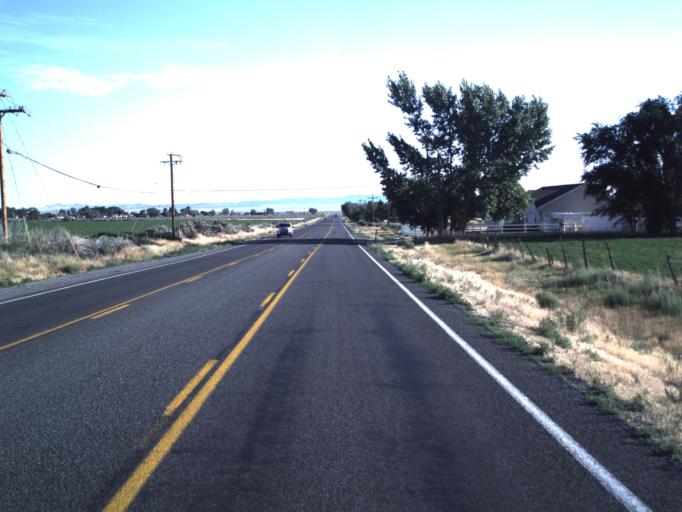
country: US
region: Utah
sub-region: Iron County
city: Enoch
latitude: 37.7496
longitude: -113.0552
